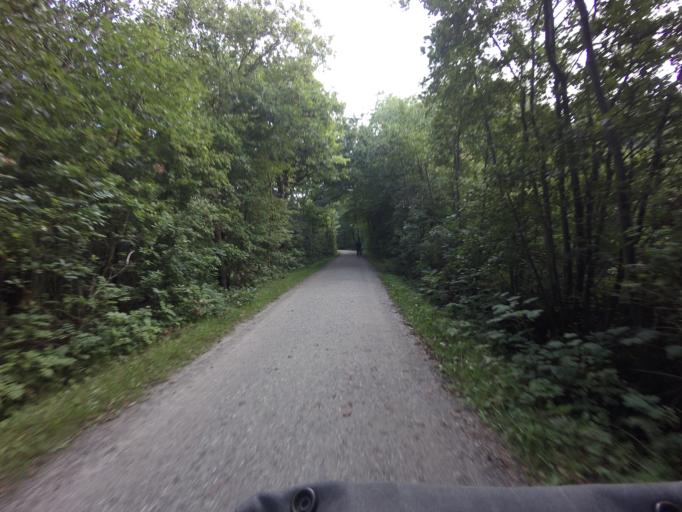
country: NL
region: Friesland
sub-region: Gemeente Terschelling
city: West-Terschelling
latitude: 53.3773
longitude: 5.2117
